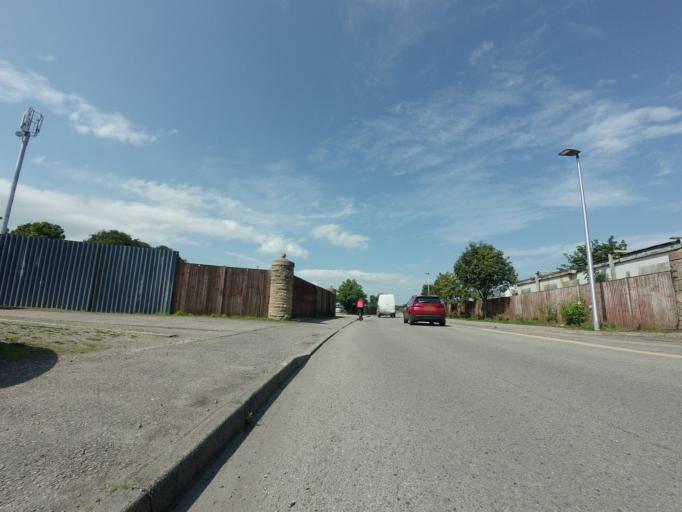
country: GB
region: Scotland
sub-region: Highland
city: Tain
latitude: 57.8154
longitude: -4.0575
